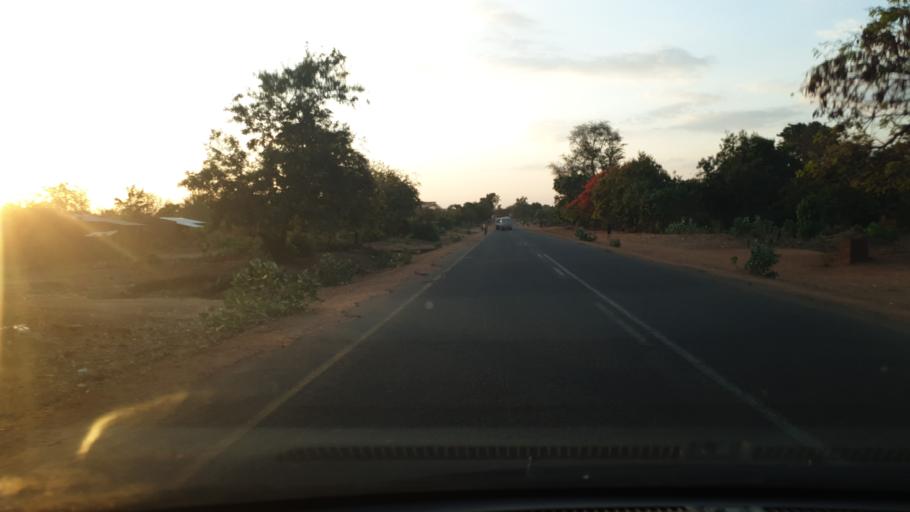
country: MW
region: Central Region
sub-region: Salima District
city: Salima
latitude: -13.7611
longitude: 34.3956
